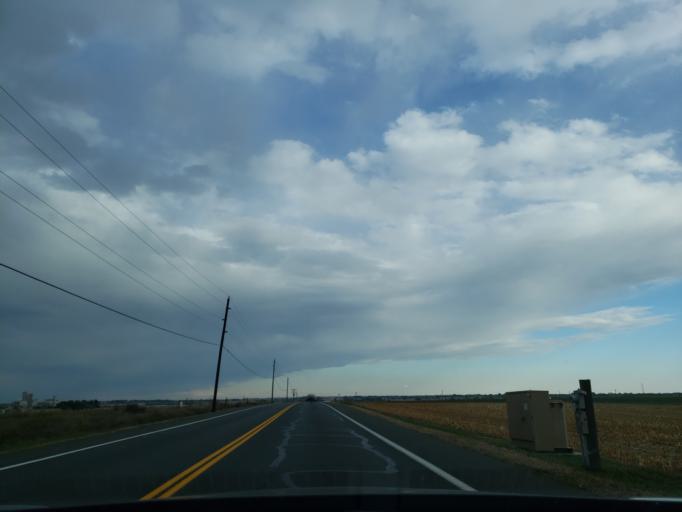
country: US
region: Colorado
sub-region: Larimer County
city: Fort Collins
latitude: 40.6102
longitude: -105.0342
